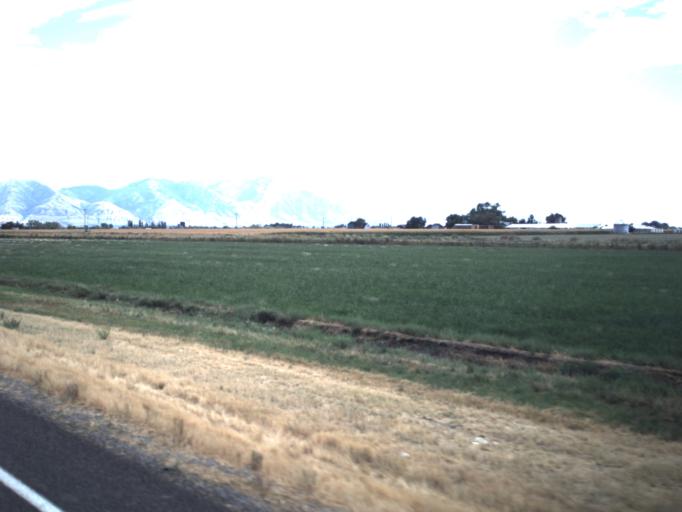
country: US
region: Utah
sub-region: Box Elder County
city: Elwood
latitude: 41.5704
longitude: -112.2034
